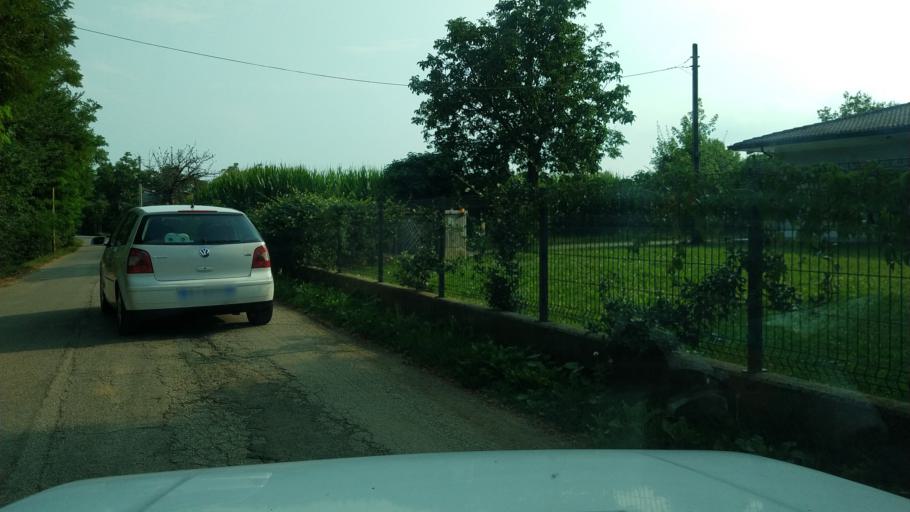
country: IT
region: Veneto
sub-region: Provincia di Vicenza
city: Nove
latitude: 45.7245
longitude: 11.6577
